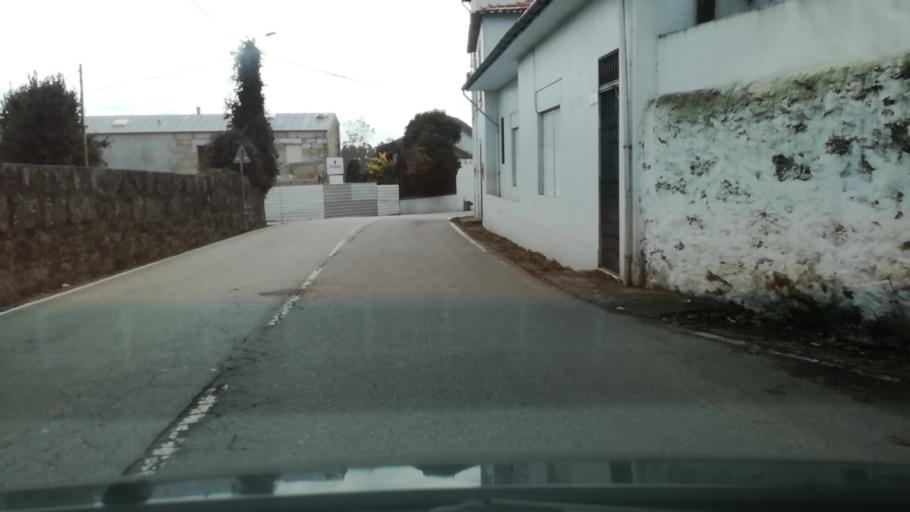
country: PT
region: Porto
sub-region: Maia
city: Maia
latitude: 41.2470
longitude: -8.6364
